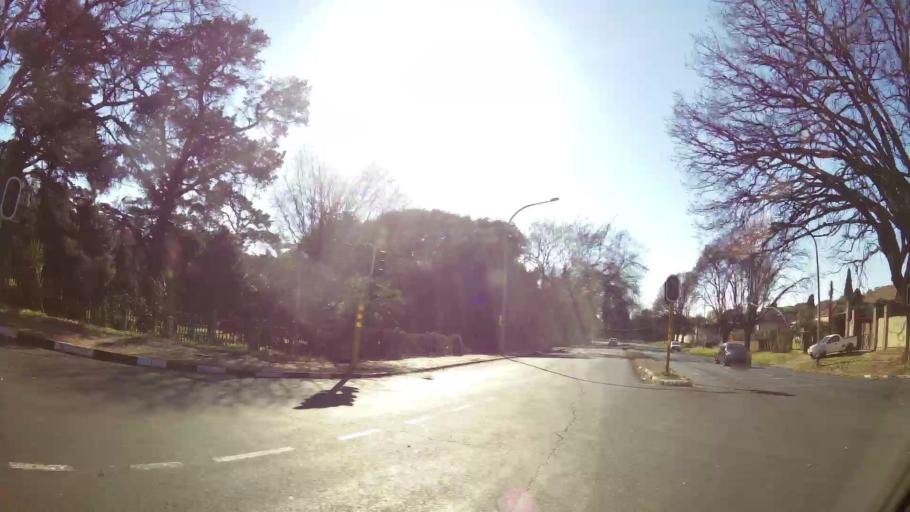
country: ZA
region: Gauteng
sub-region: City of Johannesburg Metropolitan Municipality
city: Johannesburg
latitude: -26.1970
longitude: 28.0953
